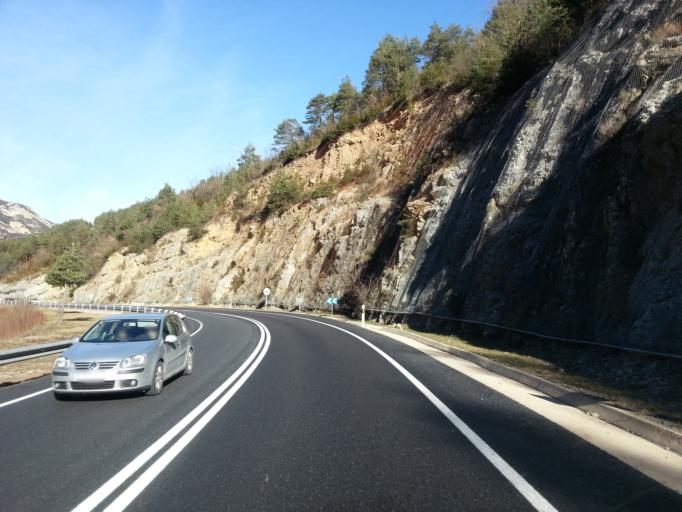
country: ES
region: Catalonia
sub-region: Provincia de Barcelona
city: Sant Julia de Cerdanyola
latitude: 42.1998
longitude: 1.8690
